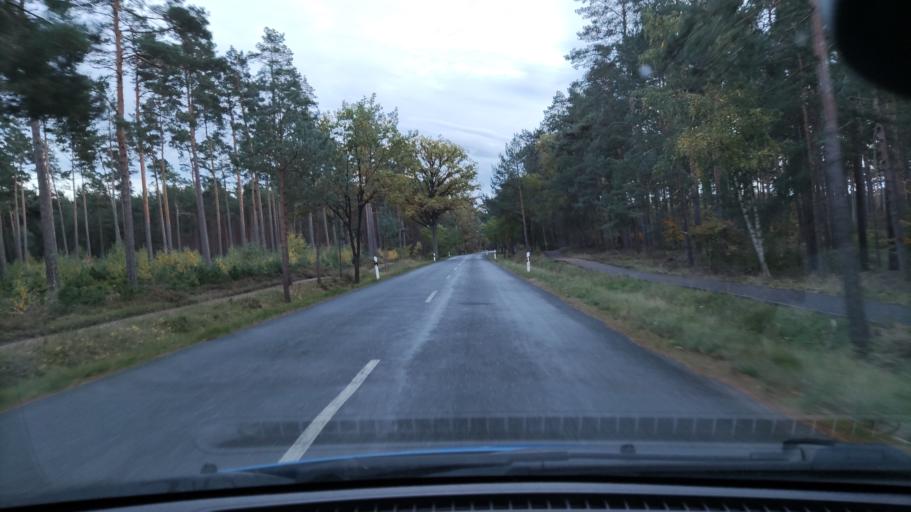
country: DE
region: Saxony-Anhalt
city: Luftkurort Arendsee
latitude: 52.9010
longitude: 11.4970
